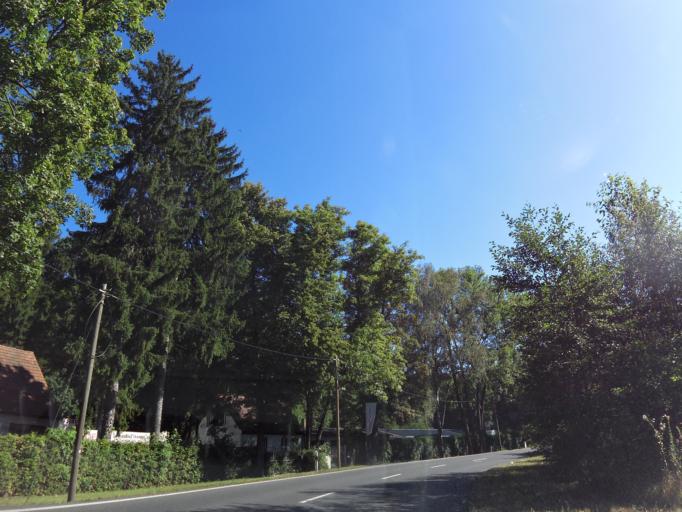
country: DE
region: Saxony
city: Dohna
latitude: 50.9438
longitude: 13.8660
